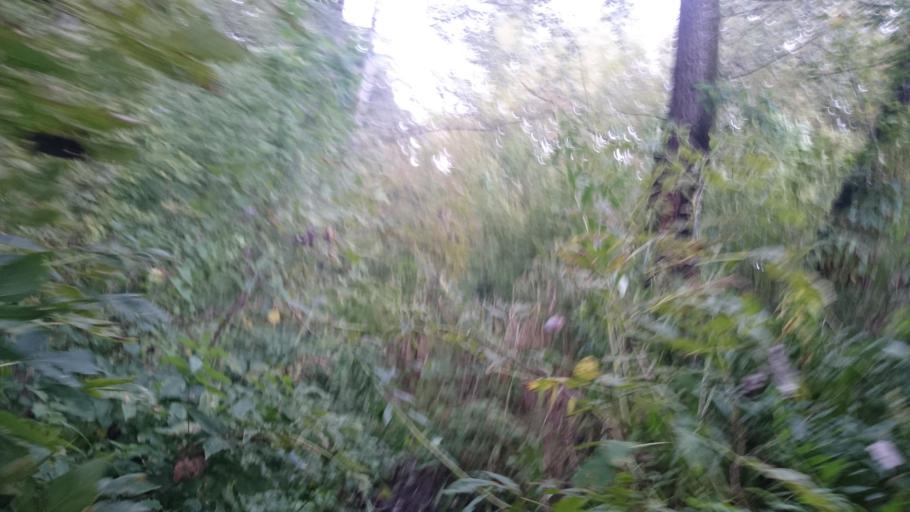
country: PL
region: Kujawsko-Pomorskie
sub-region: Grudziadz
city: Grudziadz
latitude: 53.5027
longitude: 18.7519
